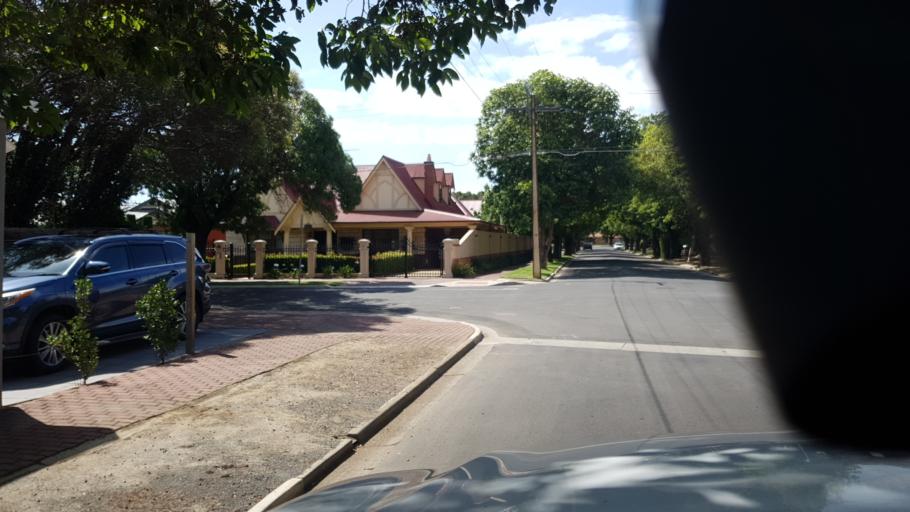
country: AU
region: South Australia
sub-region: Holdfast Bay
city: Glenelg East
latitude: -34.9776
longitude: 138.5324
